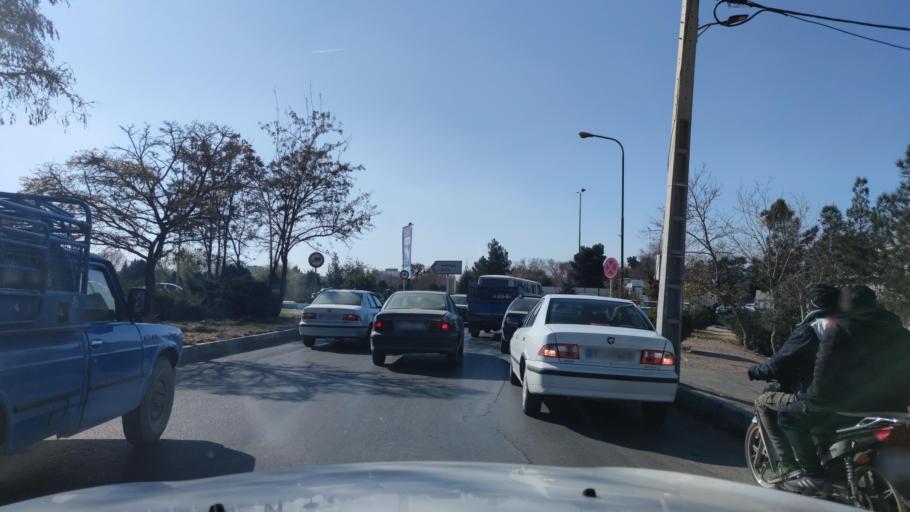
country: IR
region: Isfahan
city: Rehnan
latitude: 32.6820
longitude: 51.6422
